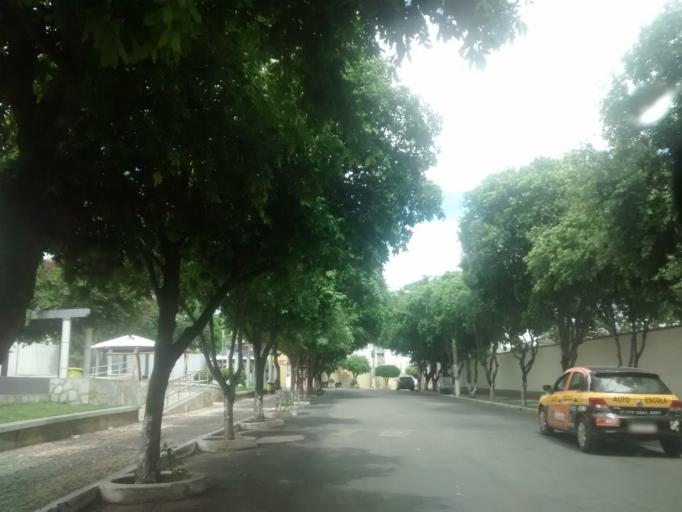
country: BR
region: Bahia
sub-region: Brumado
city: Brumado
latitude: -14.2037
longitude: -41.6691
